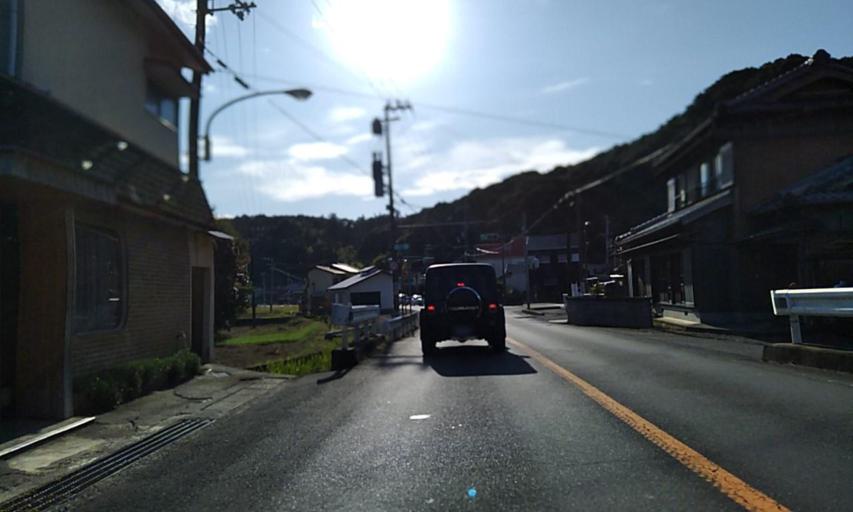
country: JP
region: Wakayama
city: Tanabe
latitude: 33.6807
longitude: 135.3895
